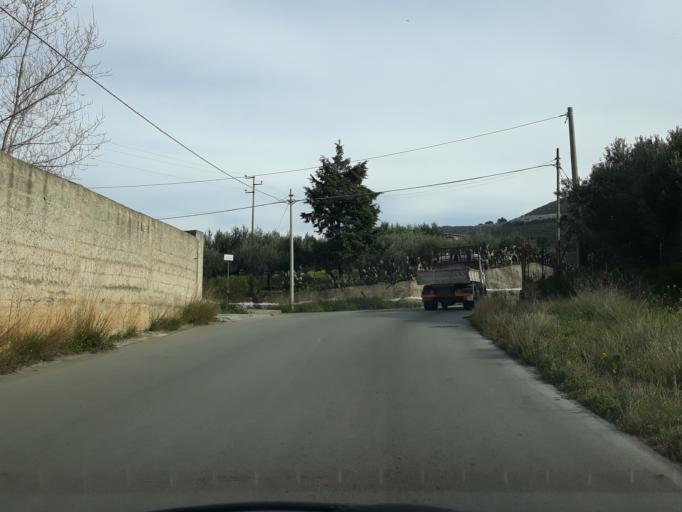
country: IT
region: Sicily
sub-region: Palermo
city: Piano Maglio-Blandino
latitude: 38.0409
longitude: 13.3201
